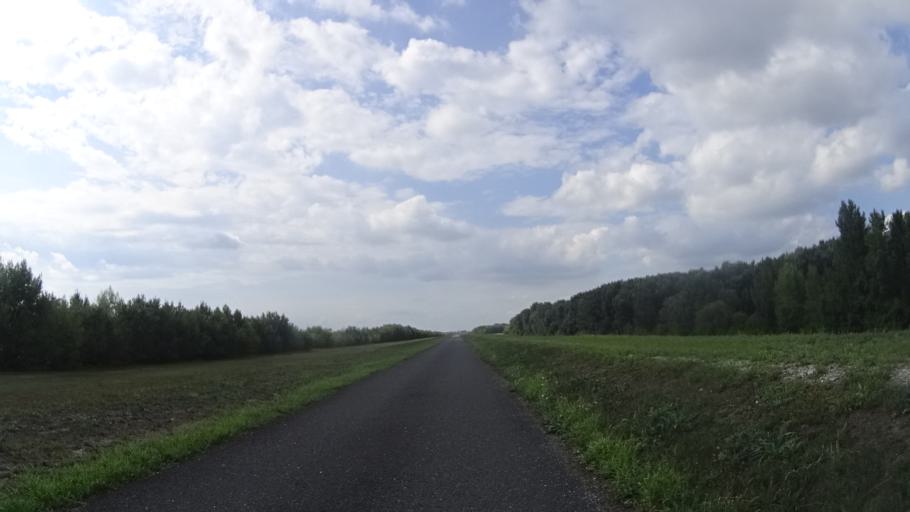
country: SK
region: Trnavsky
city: Gabcikovo
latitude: 47.8514
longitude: 17.5760
